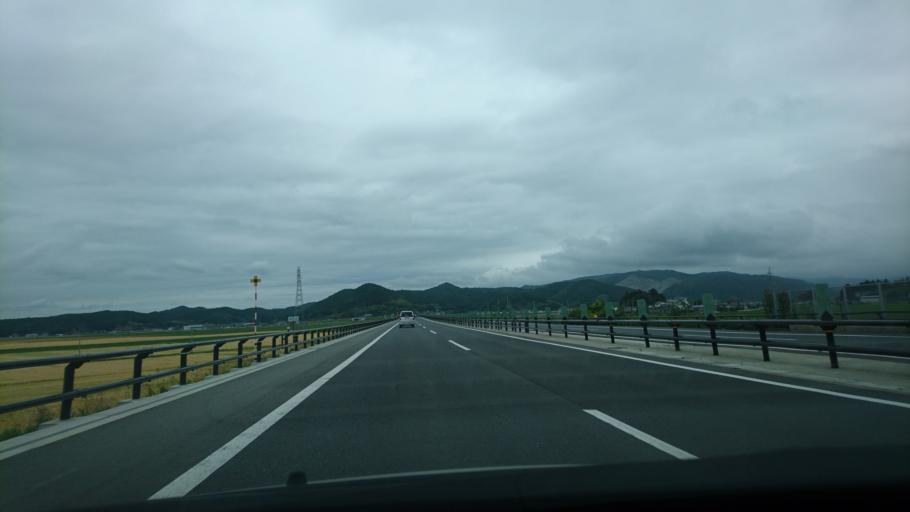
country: JP
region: Miyagi
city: Ishinomaki
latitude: 38.5092
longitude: 141.2868
